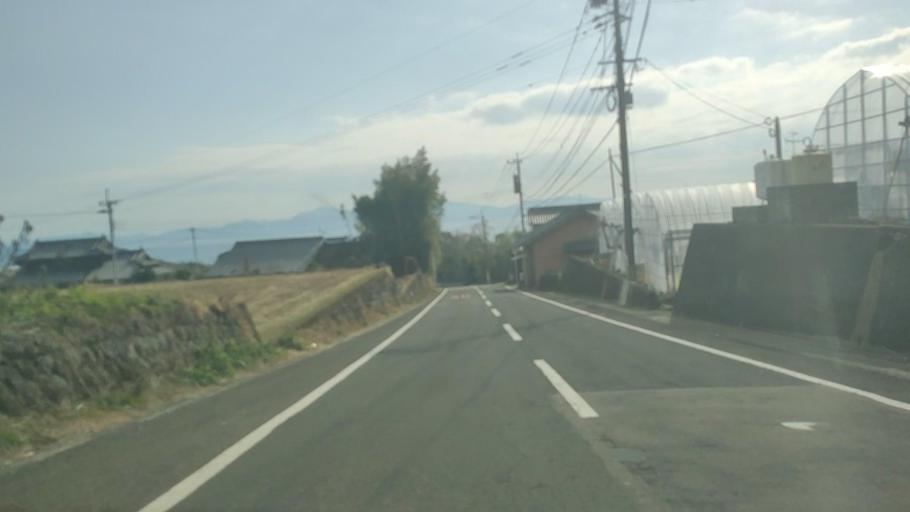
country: JP
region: Nagasaki
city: Shimabara
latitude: 32.6690
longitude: 130.2860
